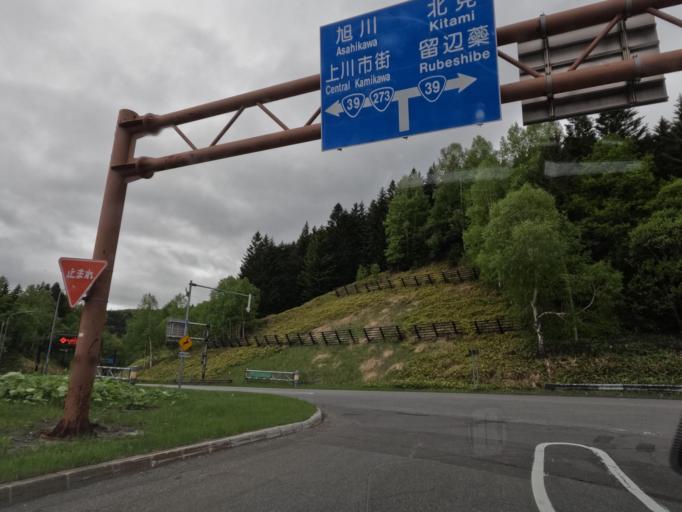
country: JP
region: Hokkaido
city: Kamikawa
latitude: 43.6806
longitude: 143.0368
